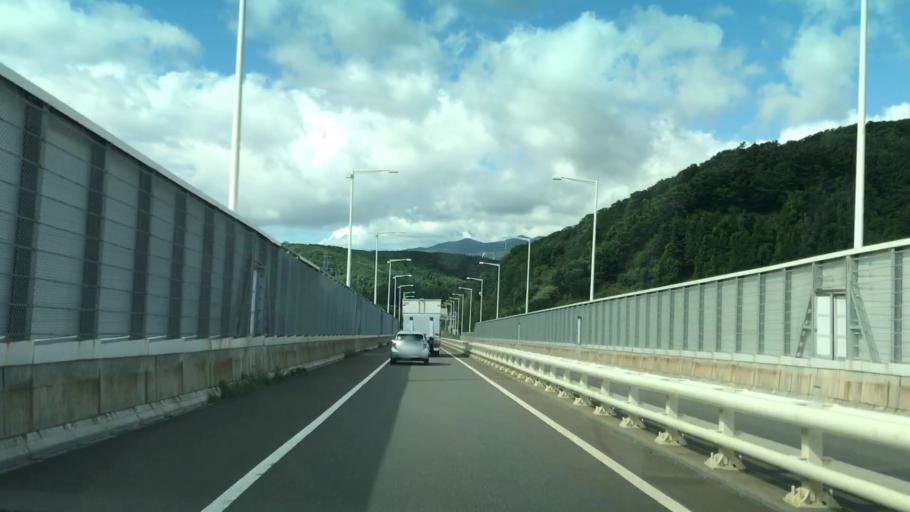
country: JP
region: Hokkaido
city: Muroran
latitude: 42.3609
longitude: 140.9514
